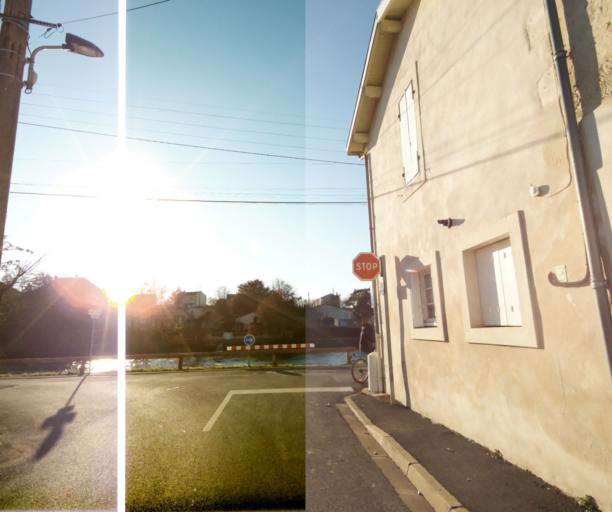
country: FR
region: Poitou-Charentes
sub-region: Departement des Deux-Sevres
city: Niort
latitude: 46.3330
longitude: -0.4785
